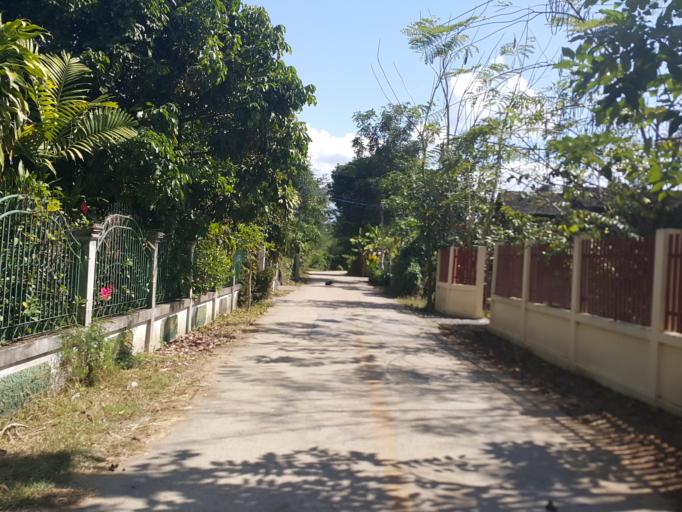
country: TH
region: Chiang Mai
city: San Kamphaeng
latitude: 18.7769
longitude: 99.1155
